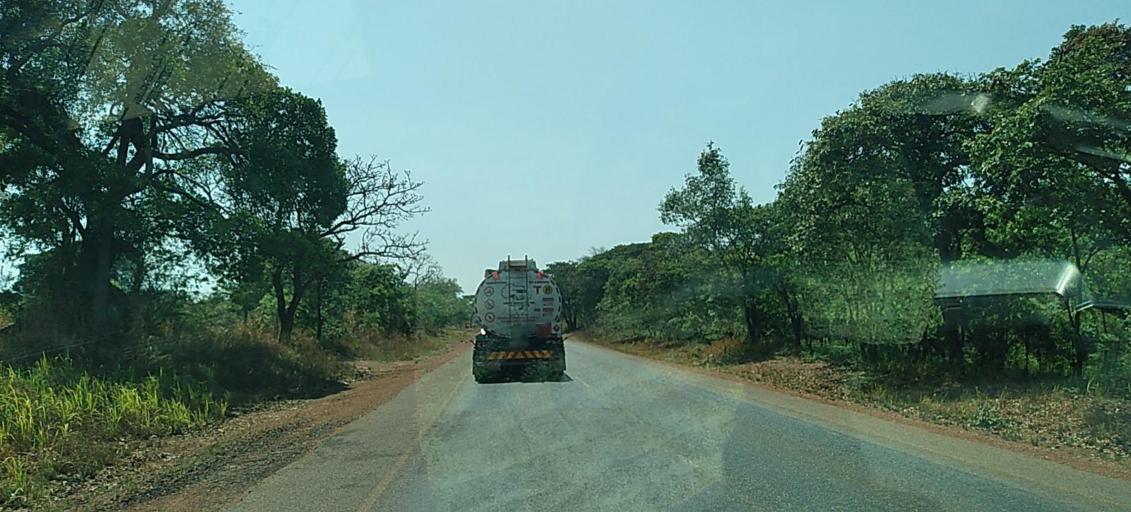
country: ZM
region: North-Western
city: Solwezi
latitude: -12.3621
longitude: 25.9655
